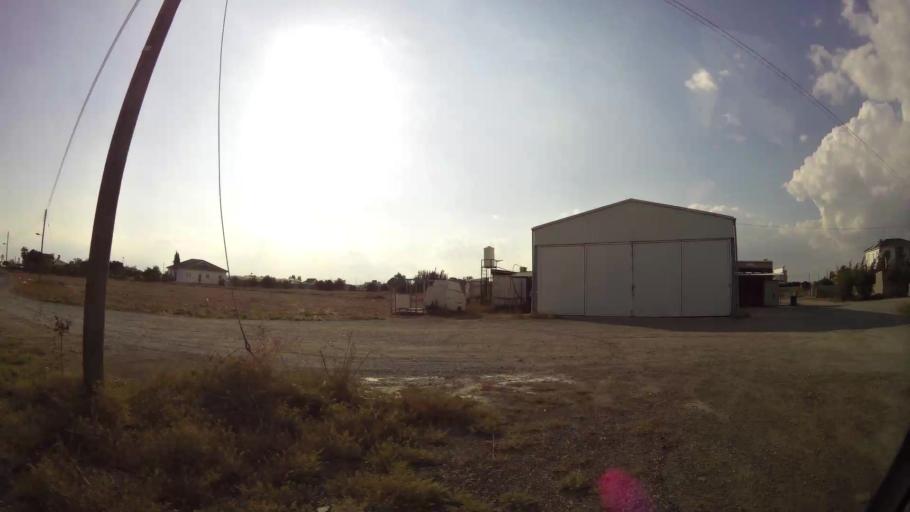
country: CY
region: Larnaka
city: Dhromolaxia
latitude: 34.8816
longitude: 33.5895
